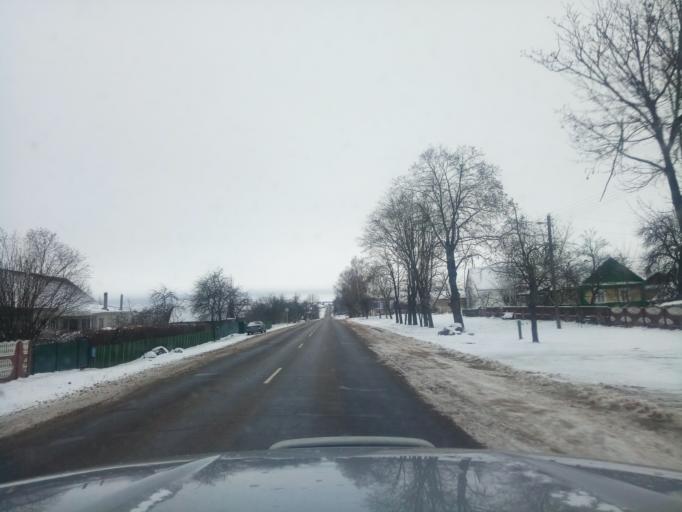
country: BY
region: Minsk
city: Kapyl'
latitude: 53.1581
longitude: 27.0981
